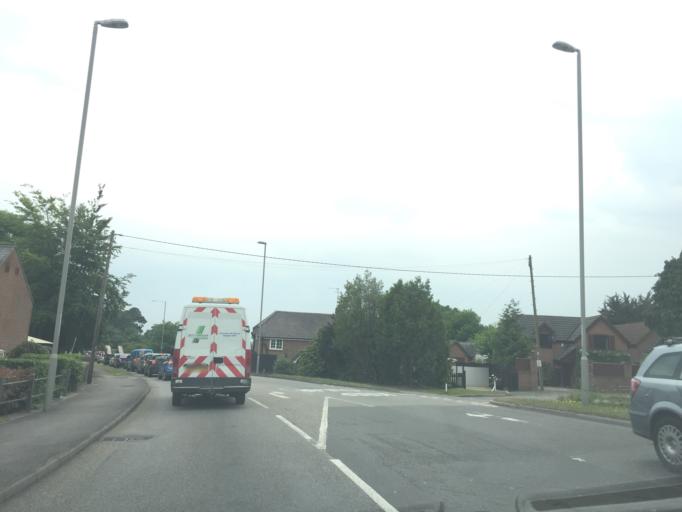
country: GB
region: England
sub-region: Dorset
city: Ferndown
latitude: 50.7918
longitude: -1.9040
